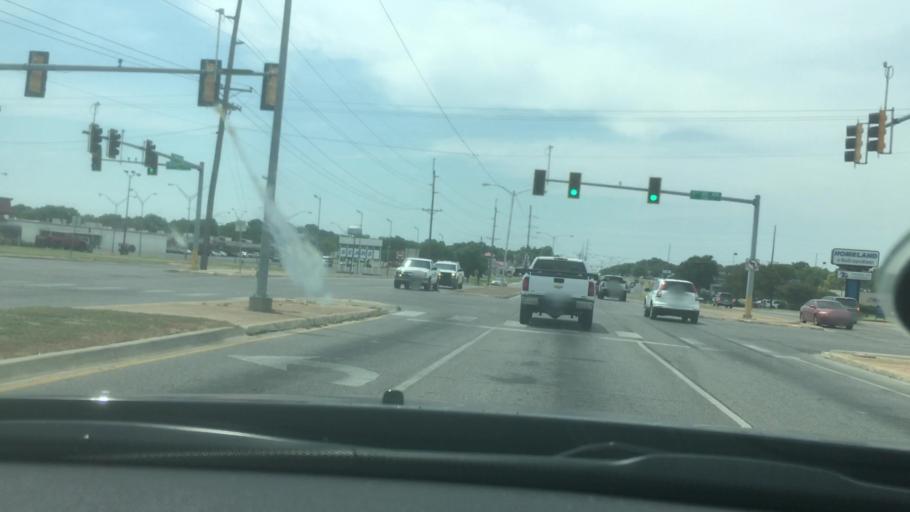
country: US
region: Oklahoma
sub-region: Carter County
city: Ardmore
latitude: 34.1806
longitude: -97.1431
